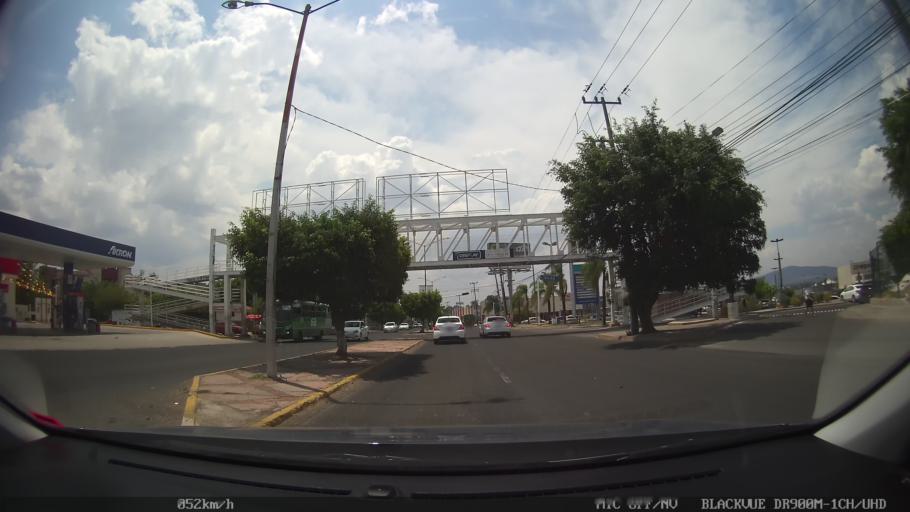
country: MX
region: Jalisco
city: Tlaquepaque
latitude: 20.6388
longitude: -103.2754
